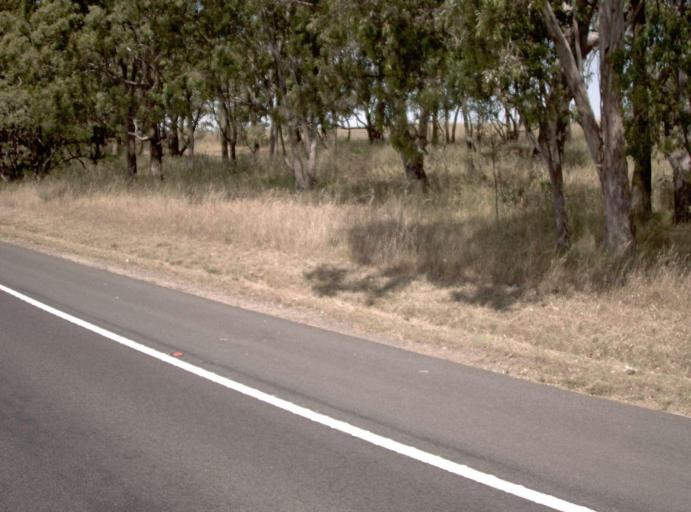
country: AU
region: Victoria
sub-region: Latrobe
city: Traralgon
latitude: -38.1802
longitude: 146.6220
